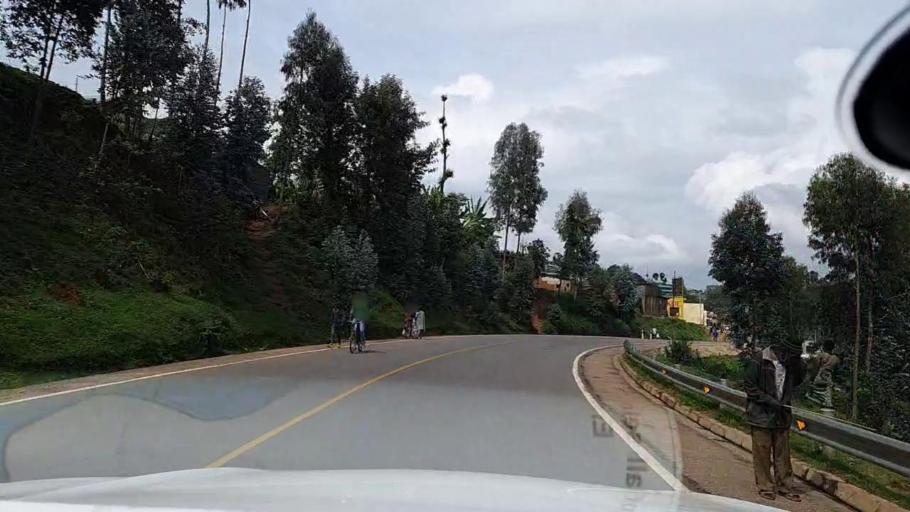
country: RW
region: Southern Province
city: Nzega
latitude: -2.4851
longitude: 29.5300
